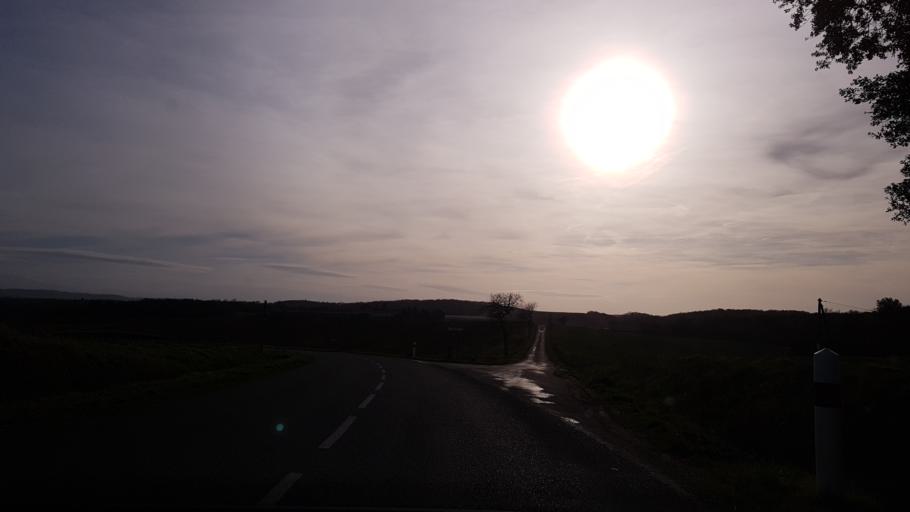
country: FR
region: Languedoc-Roussillon
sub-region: Departement de l'Aude
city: Villeneuve-la-Comptal
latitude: 43.2266
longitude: 1.9188
